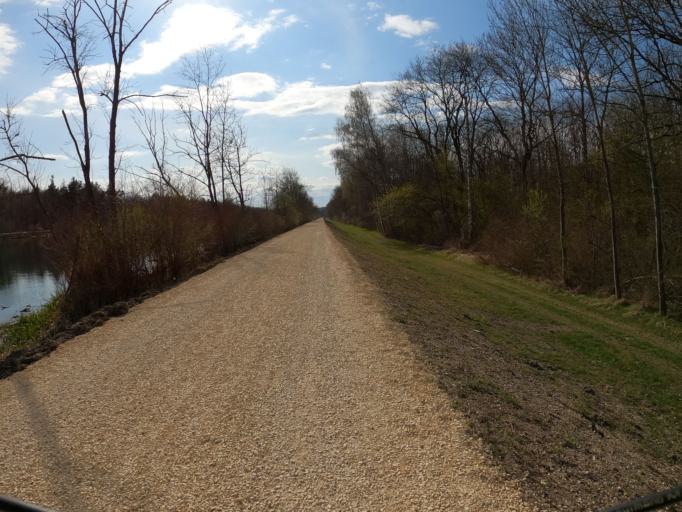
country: DE
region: Bavaria
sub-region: Swabia
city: Nersingen
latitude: 48.4378
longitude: 10.0898
